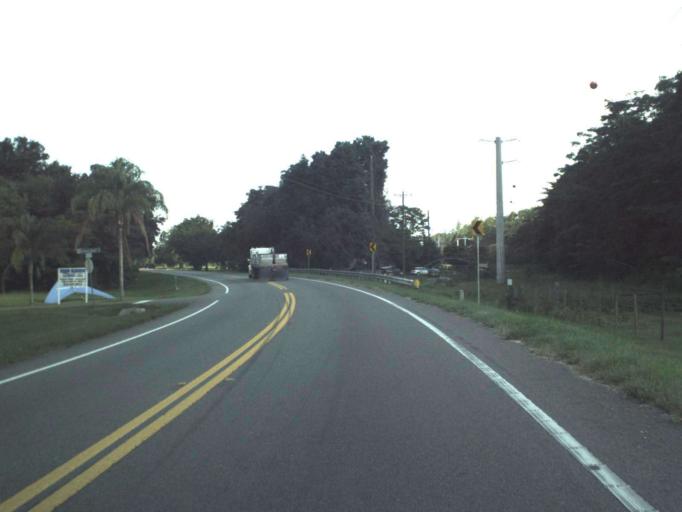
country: US
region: Florida
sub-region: Lake County
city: Groveland
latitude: 28.5367
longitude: -81.8515
